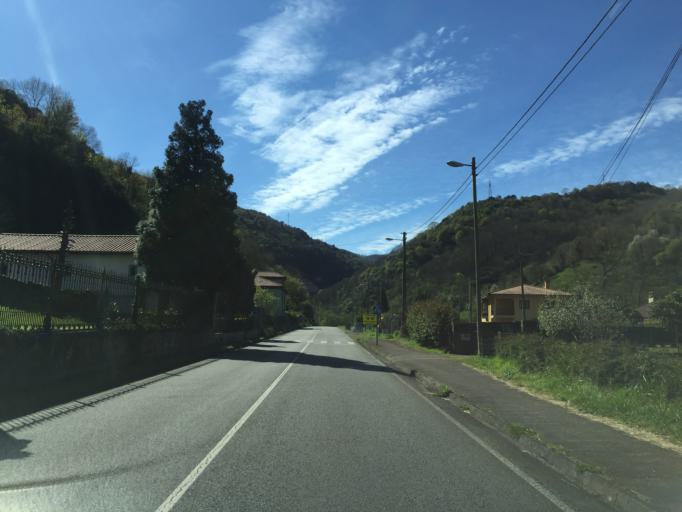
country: ES
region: Asturias
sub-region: Province of Asturias
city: Proaza
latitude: 43.3121
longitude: -5.9882
